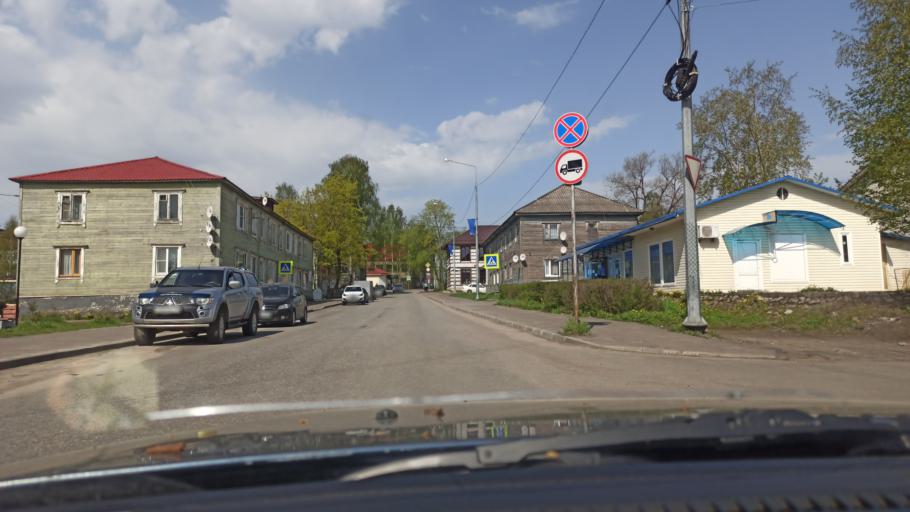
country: RU
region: Republic of Karelia
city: Lakhdenpokh'ya
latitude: 61.5188
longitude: 30.1997
